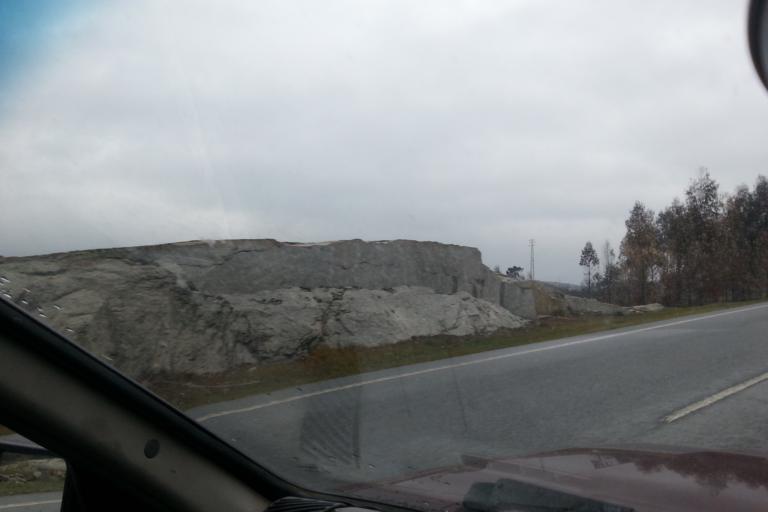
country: PT
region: Viseu
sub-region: Mangualde
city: Mangualde
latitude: 40.6010
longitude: -7.8108
